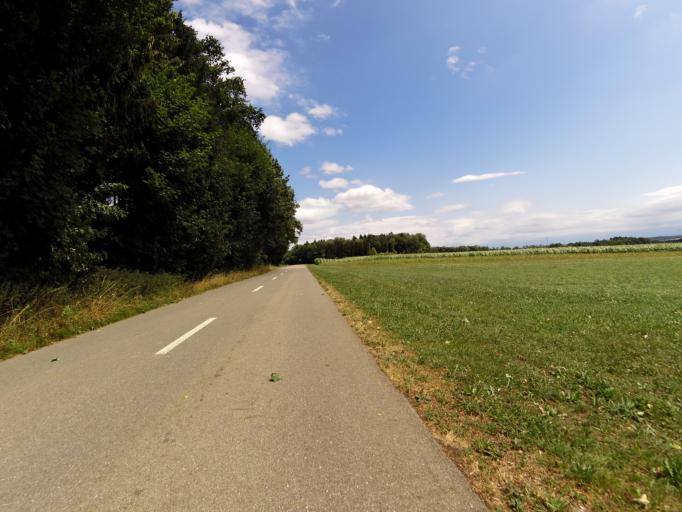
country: CH
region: Thurgau
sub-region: Weinfelden District
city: Maerstetten-Dorf
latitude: 47.6236
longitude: 9.0886
